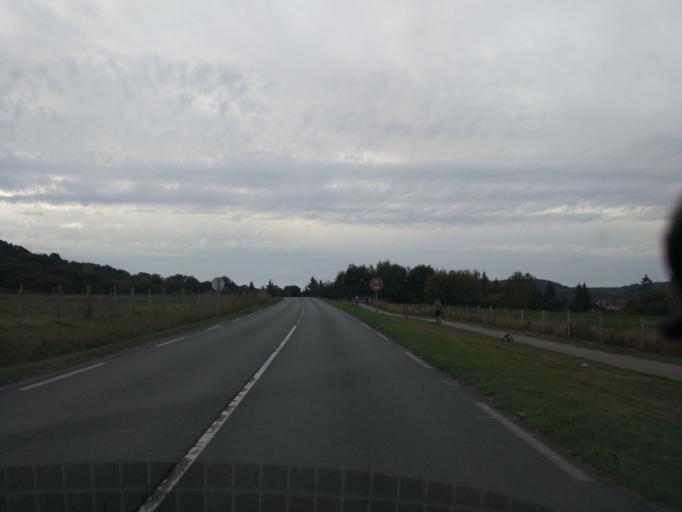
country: FR
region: Ile-de-France
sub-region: Departement des Yvelines
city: Chevreuse
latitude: 48.7022
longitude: 2.0508
